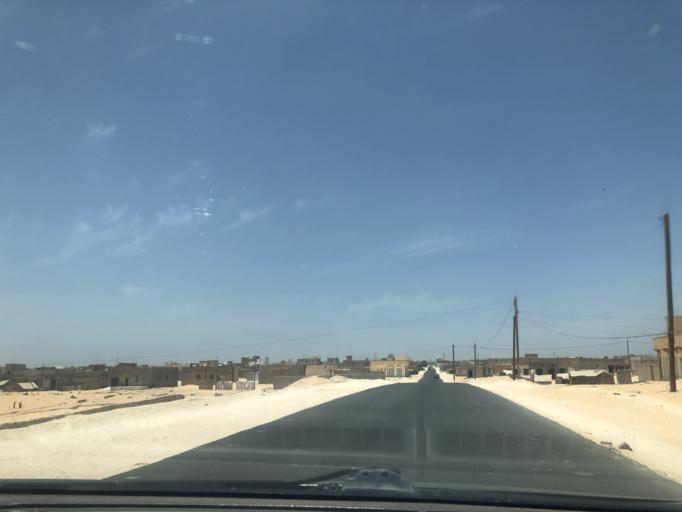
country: MR
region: Nouakchott
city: Nouakchott
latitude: 18.0037
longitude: -15.9604
